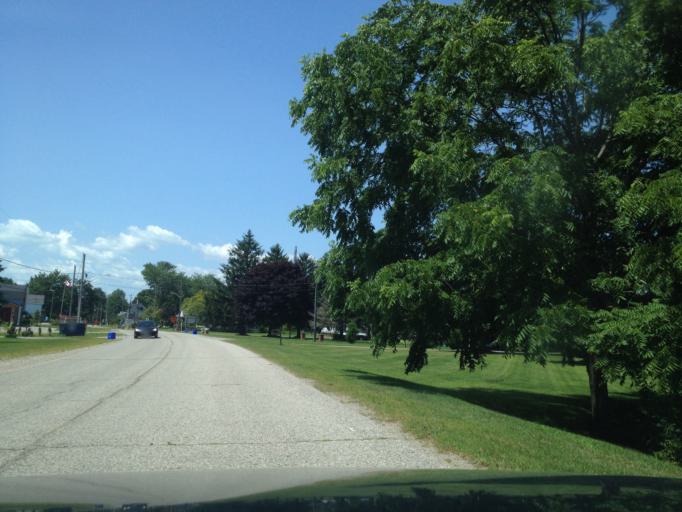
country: CA
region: Ontario
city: Aylmer
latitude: 42.6465
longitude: -80.7971
